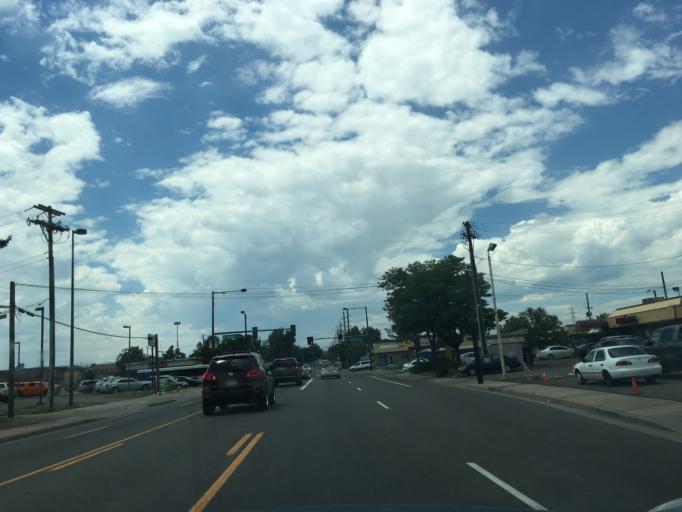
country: US
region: Colorado
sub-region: Arapahoe County
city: Sheridan
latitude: 39.6968
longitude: -105.0240
